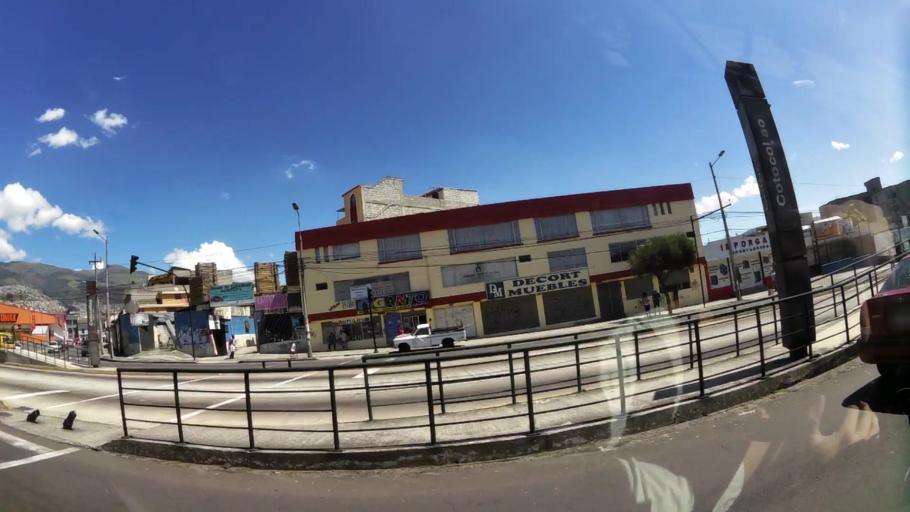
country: EC
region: Pichincha
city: Quito
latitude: -0.1193
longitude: -78.4923
